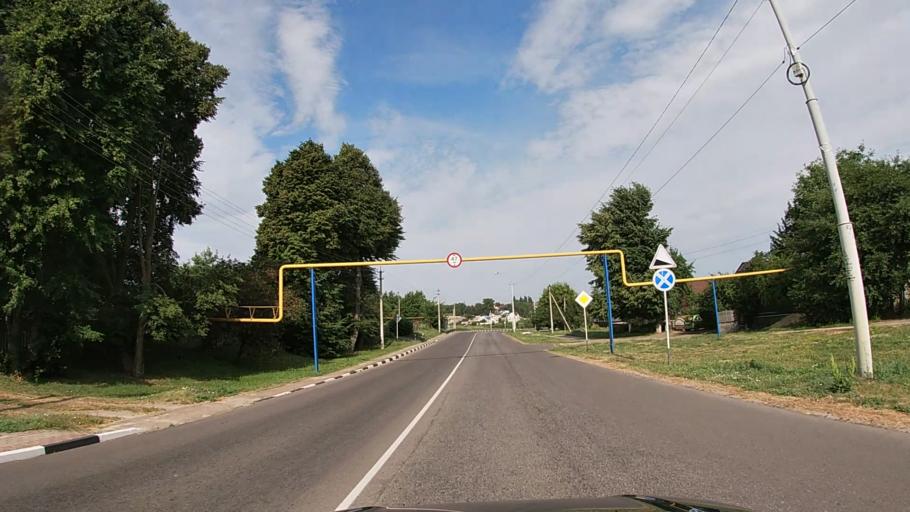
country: RU
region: Belgorod
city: Krasnaya Yaruga
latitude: 50.8000
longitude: 35.6741
